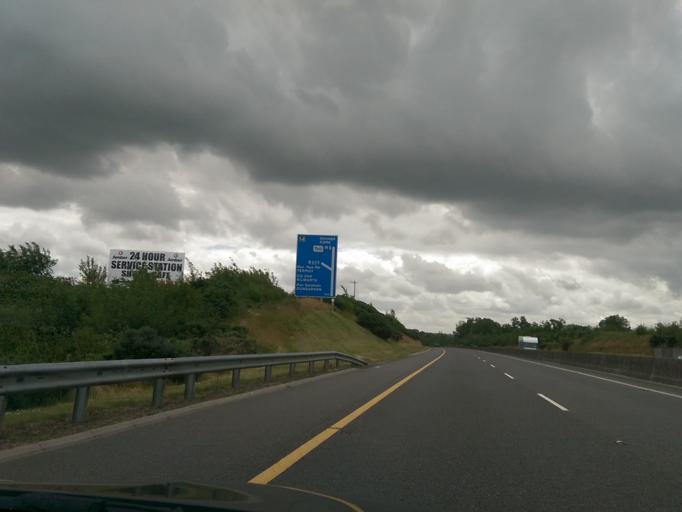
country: IE
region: Munster
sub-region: County Cork
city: Fermoy
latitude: 52.1801
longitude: -8.2717
